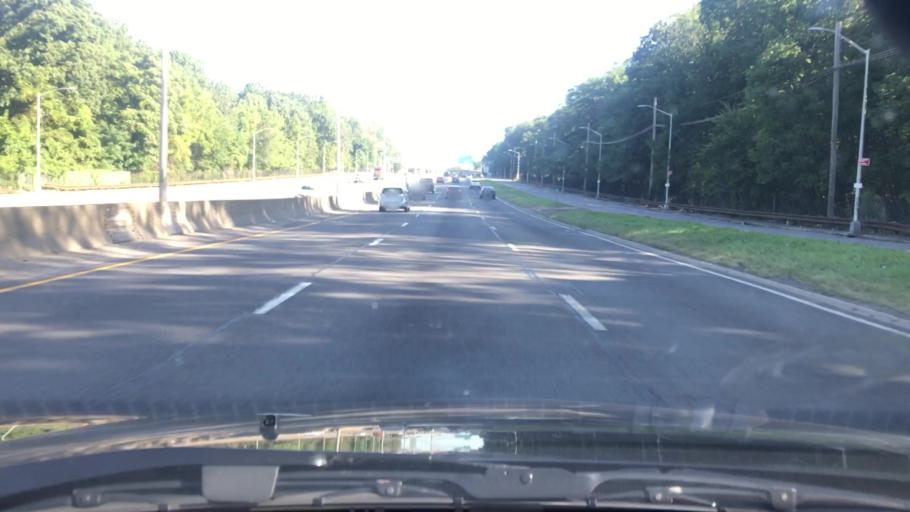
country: US
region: New York
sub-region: Westchester County
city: Yonkers
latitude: 40.9004
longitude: -73.8789
